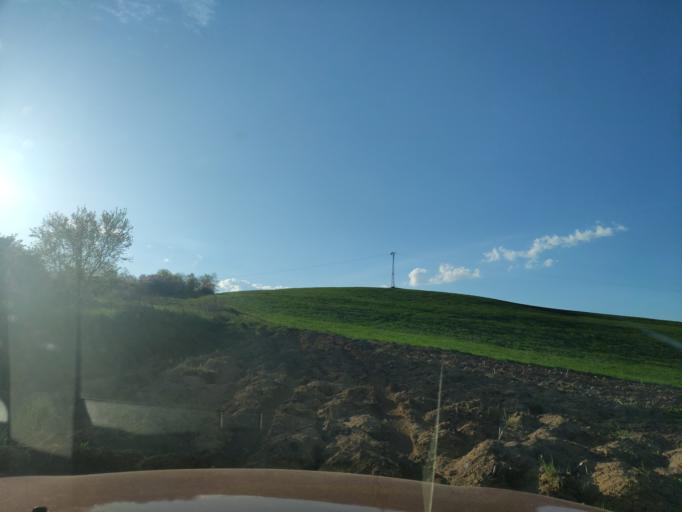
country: SK
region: Presovsky
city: Lipany
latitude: 49.1510
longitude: 20.8576
